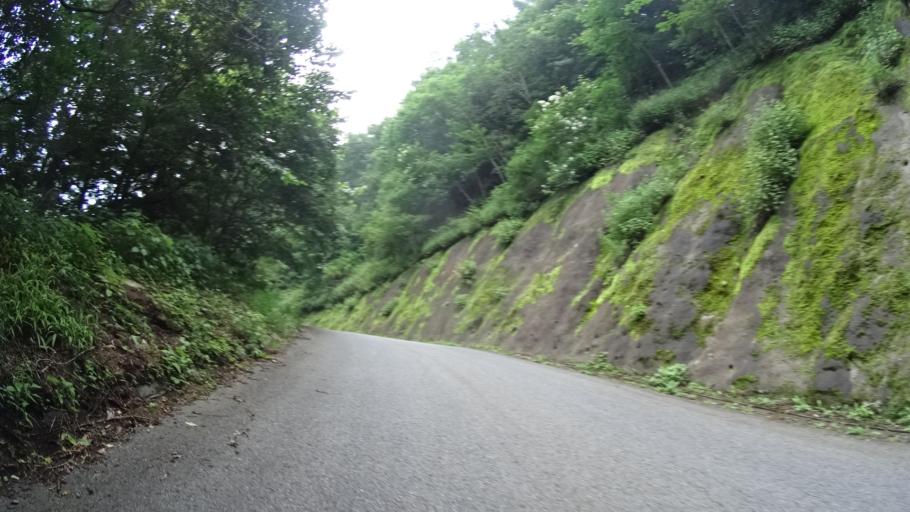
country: JP
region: Nagano
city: Saku
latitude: 36.0928
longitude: 138.6811
